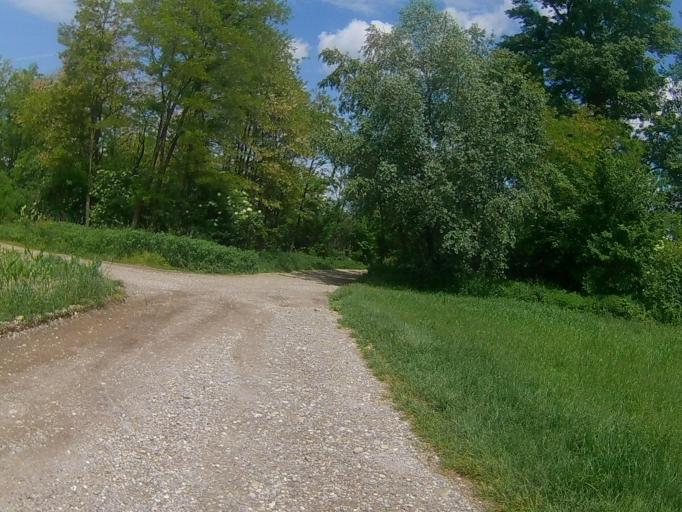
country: SI
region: Starse
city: Starse
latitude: 46.4604
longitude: 15.7940
